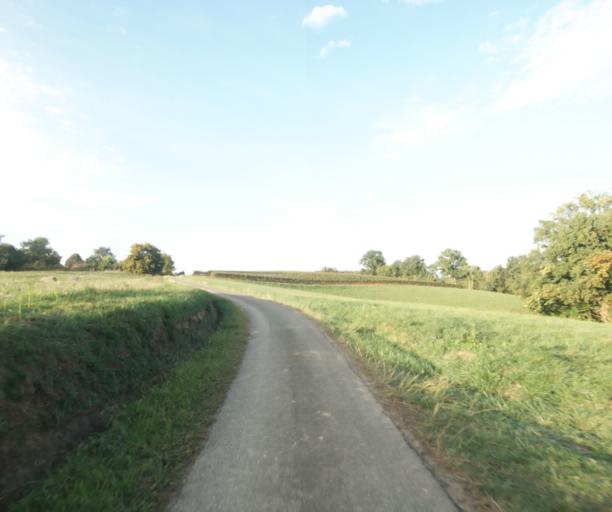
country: FR
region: Midi-Pyrenees
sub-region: Departement du Gers
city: Le Houga
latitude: 43.8369
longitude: -0.1150
